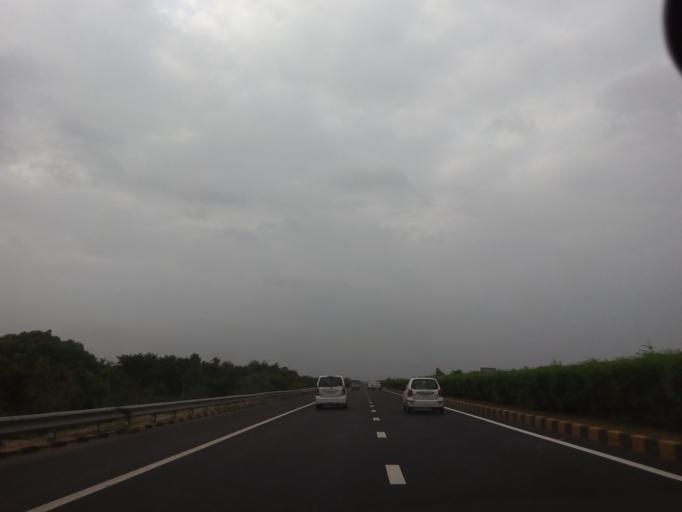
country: IN
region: Gujarat
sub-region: Kheda
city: Chaklasi
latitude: 22.6418
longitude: 72.9364
